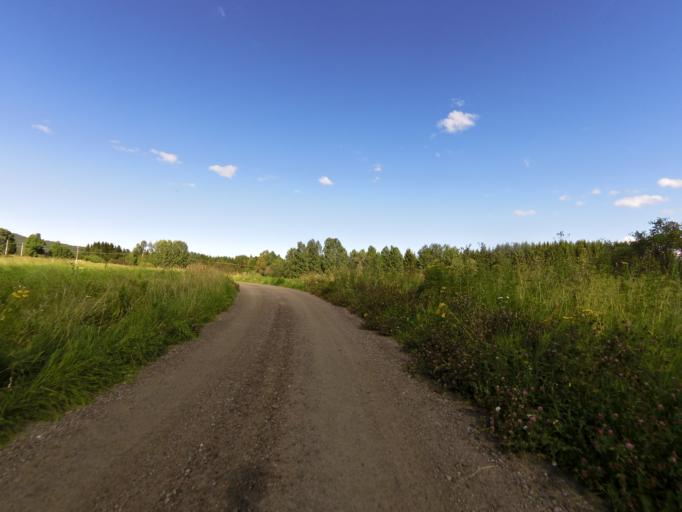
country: SE
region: Gaevleborg
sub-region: Hofors Kommun
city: Hofors
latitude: 60.5141
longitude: 16.4159
